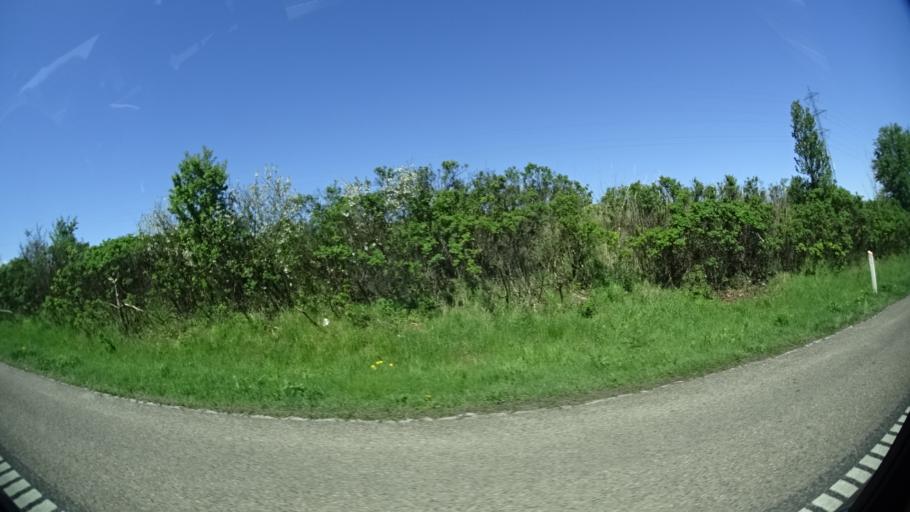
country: DK
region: Central Jutland
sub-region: Arhus Kommune
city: Stavtrup
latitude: 56.1250
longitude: 10.1180
